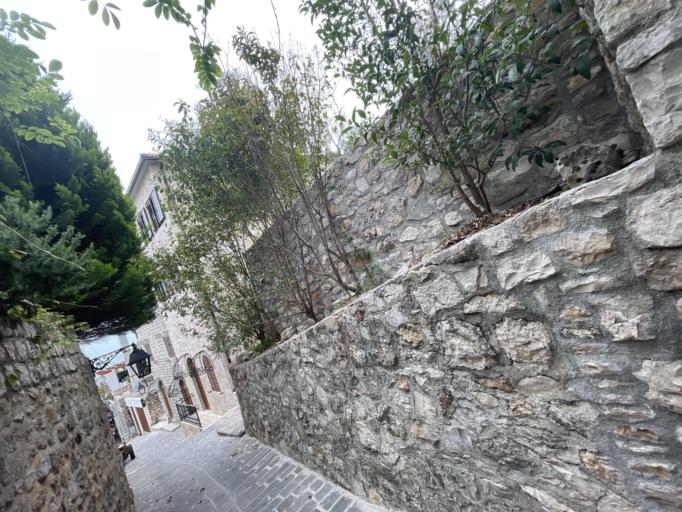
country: ME
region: Ulcinj
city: Ulcinj
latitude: 41.9236
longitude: 19.2016
